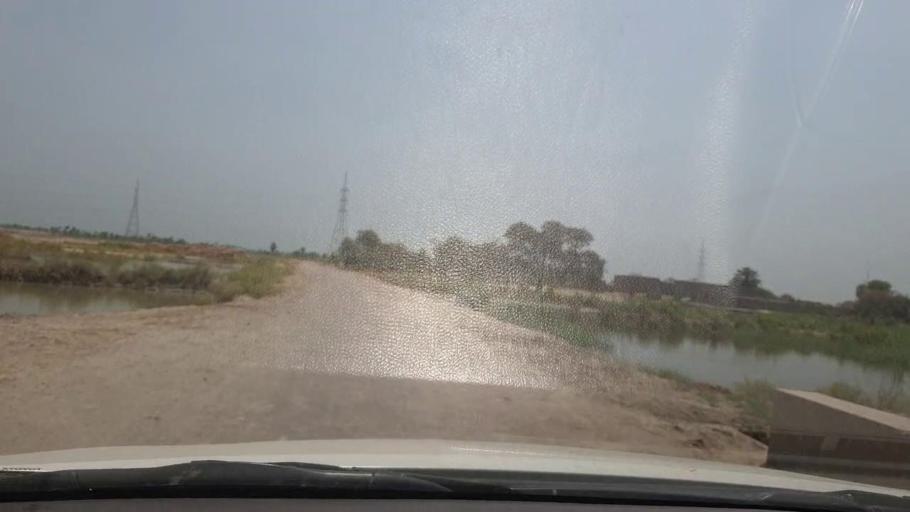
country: PK
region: Sindh
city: Shikarpur
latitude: 28.0949
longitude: 68.6139
